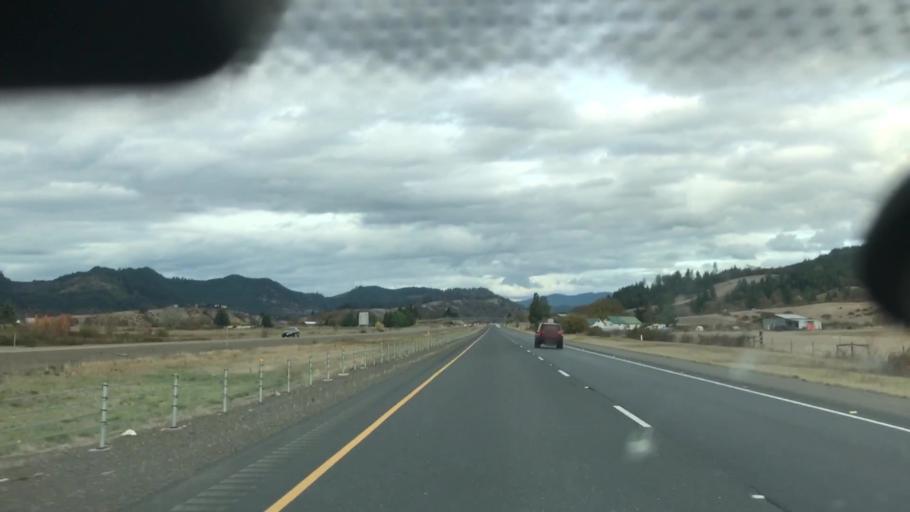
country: US
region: Oregon
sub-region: Douglas County
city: Yoncalla
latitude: 43.5744
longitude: -123.2680
